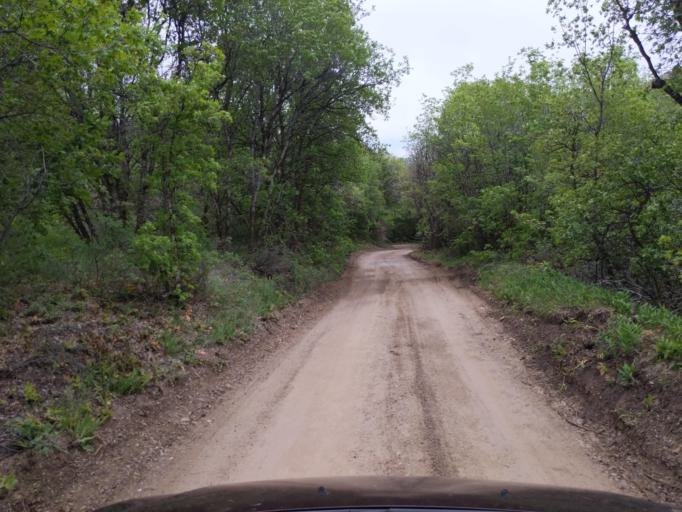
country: US
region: Idaho
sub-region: Bannock County
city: Pocatello
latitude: 42.8278
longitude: -112.4824
